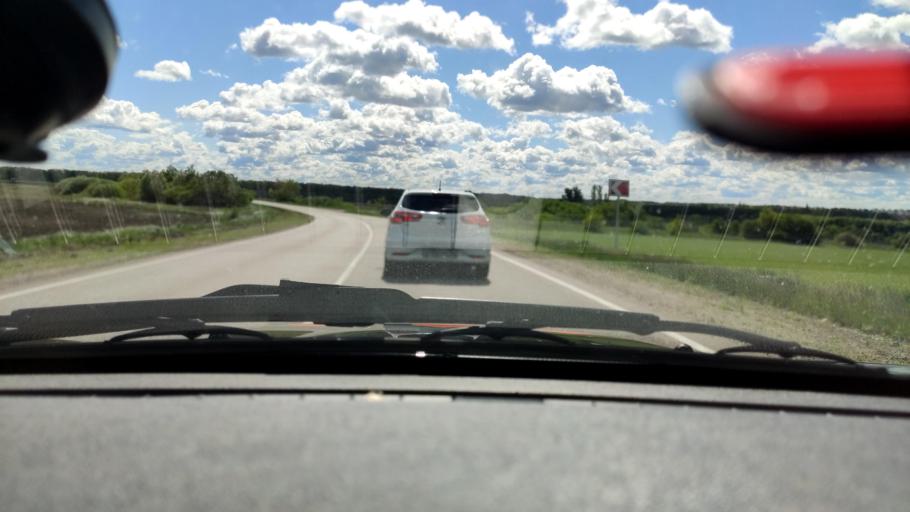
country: RU
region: Voronezj
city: Shilovo
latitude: 51.4530
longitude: 38.9756
